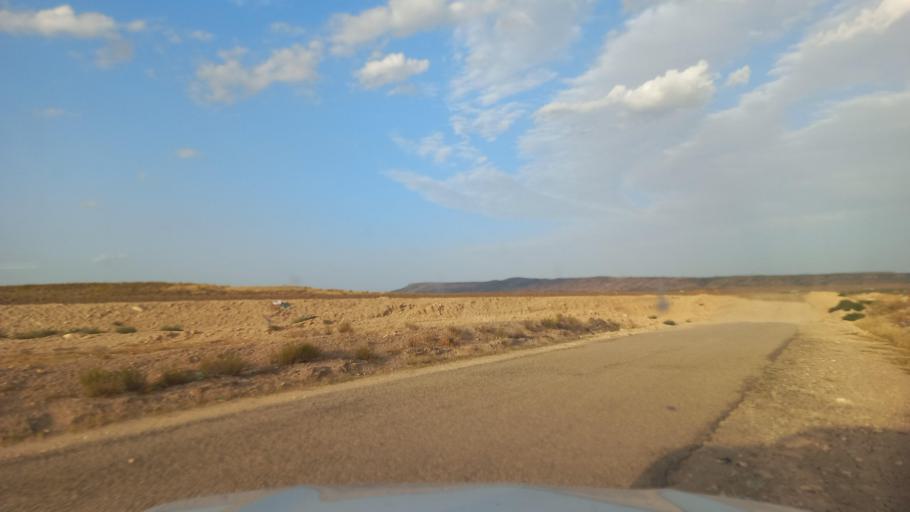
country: TN
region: Al Qasrayn
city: Sbiba
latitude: 35.3091
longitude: 9.0741
